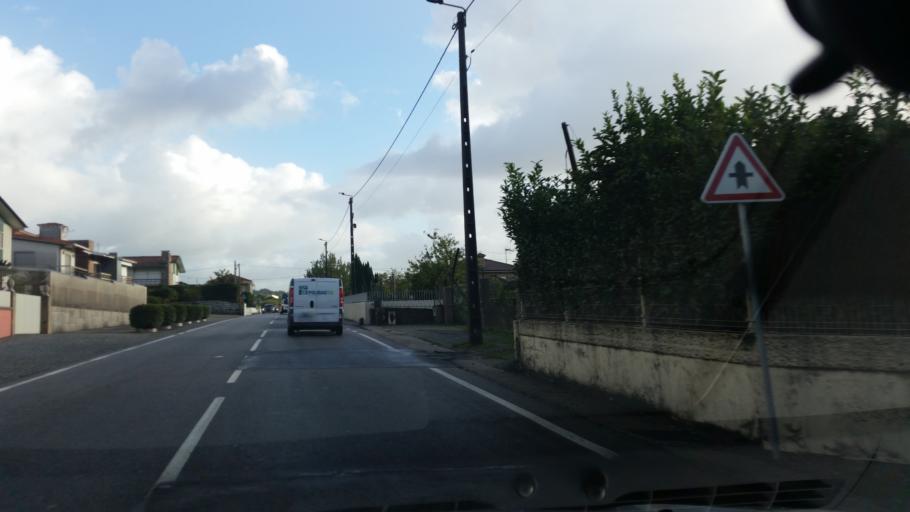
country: PT
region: Braga
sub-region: Guimaraes
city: Lordelo
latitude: 41.3653
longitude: -8.3933
